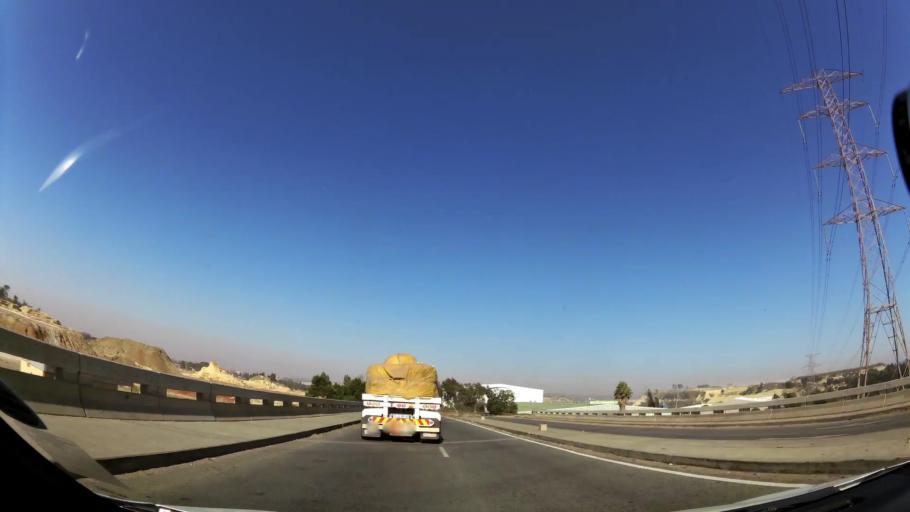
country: ZA
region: Gauteng
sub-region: Ekurhuleni Metropolitan Municipality
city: Germiston
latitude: -26.2114
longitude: 28.1160
